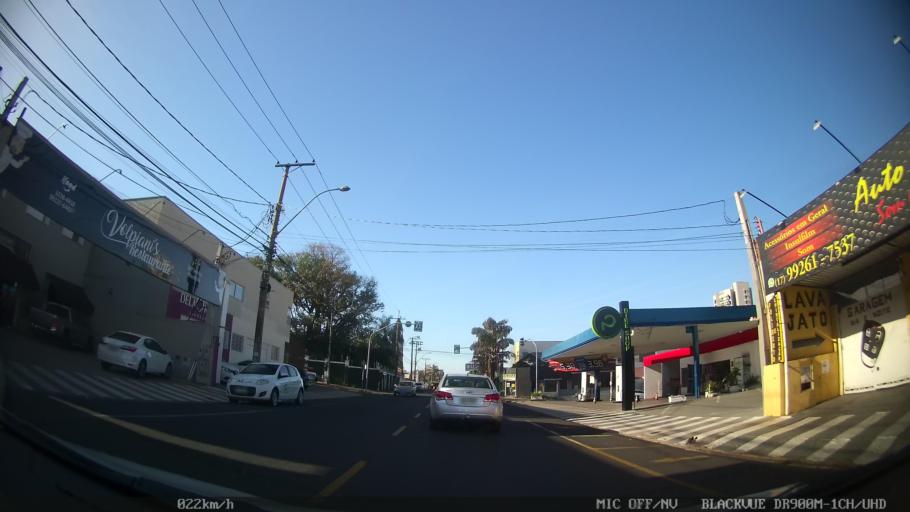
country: BR
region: Sao Paulo
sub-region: Sao Jose Do Rio Preto
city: Sao Jose do Rio Preto
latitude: -20.8090
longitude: -49.3890
